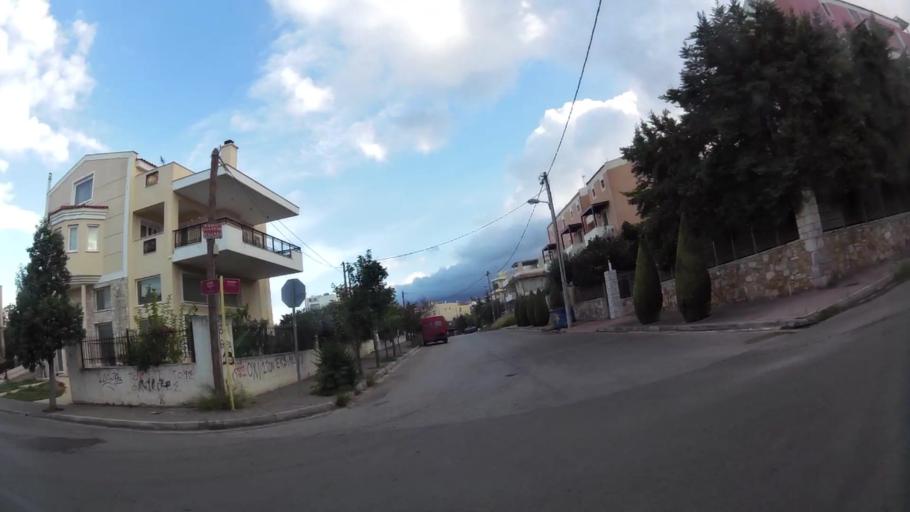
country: GR
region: Attica
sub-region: Nomarchia Athinas
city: Marousi
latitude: 38.0429
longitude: 23.8146
